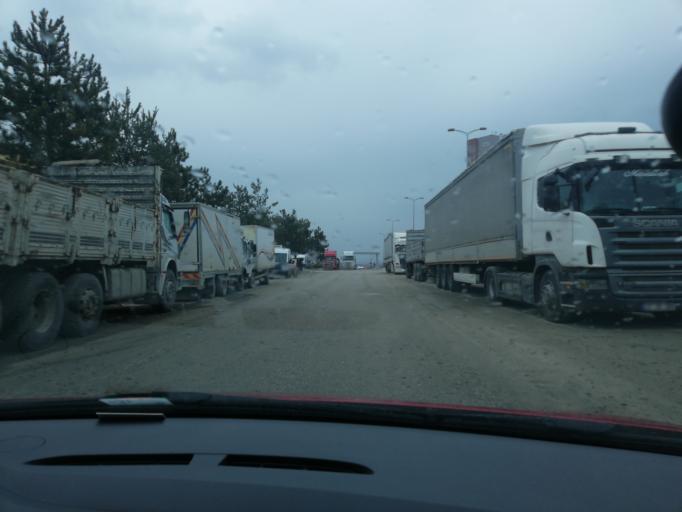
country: TR
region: Kastamonu
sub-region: Cide
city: Kastamonu
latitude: 41.4171
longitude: 33.7769
